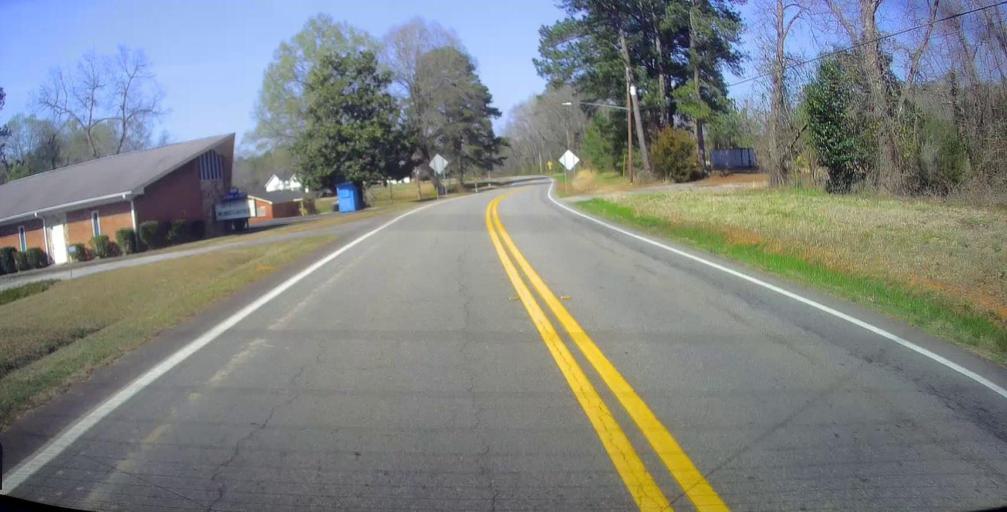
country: US
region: Georgia
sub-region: Jones County
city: Gray
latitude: 33.0120
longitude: -83.5343
